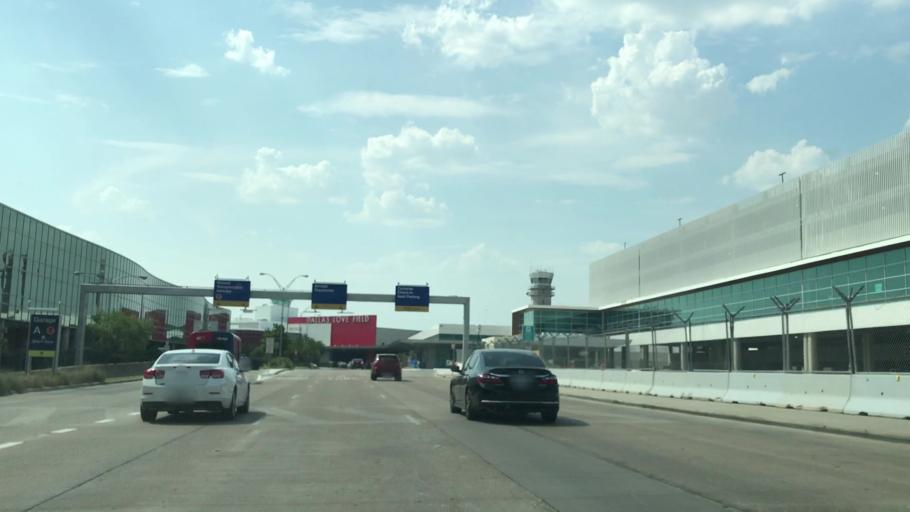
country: US
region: Texas
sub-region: Dallas County
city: University Park
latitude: 32.8422
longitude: -96.8472
